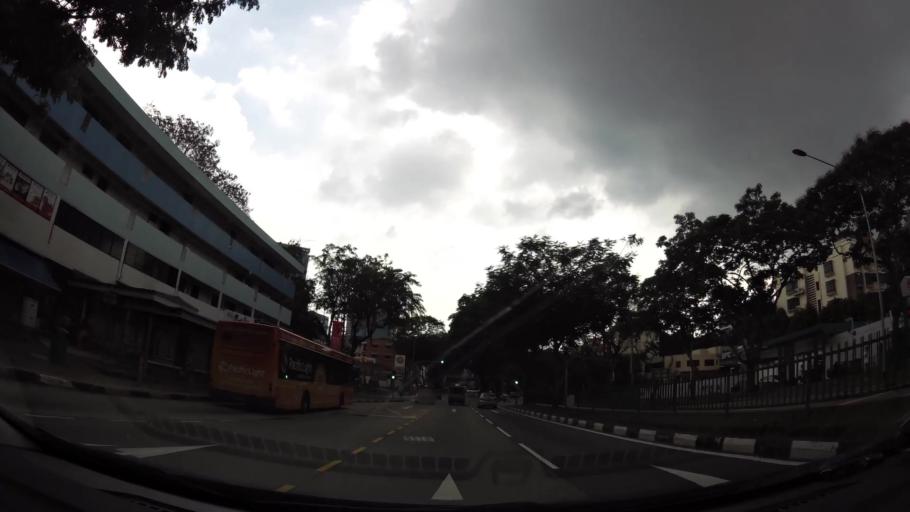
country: SG
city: Singapore
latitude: 1.3250
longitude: 103.8420
